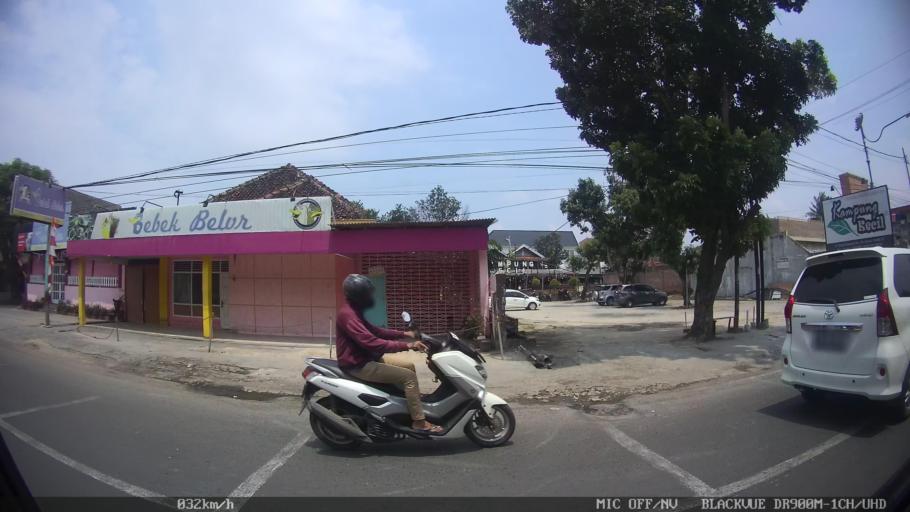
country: ID
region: Lampung
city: Bandarlampung
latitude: -5.4289
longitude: 105.2757
